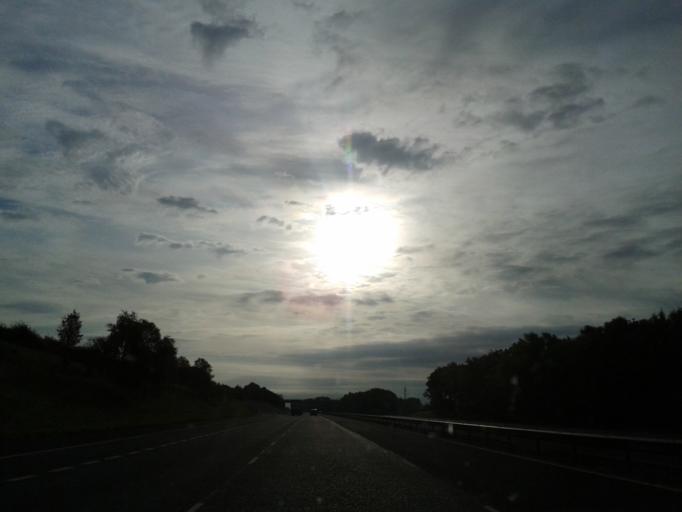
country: GB
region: Scotland
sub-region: Dumfries and Galloway
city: Gretna
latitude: 55.0118
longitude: -3.0952
